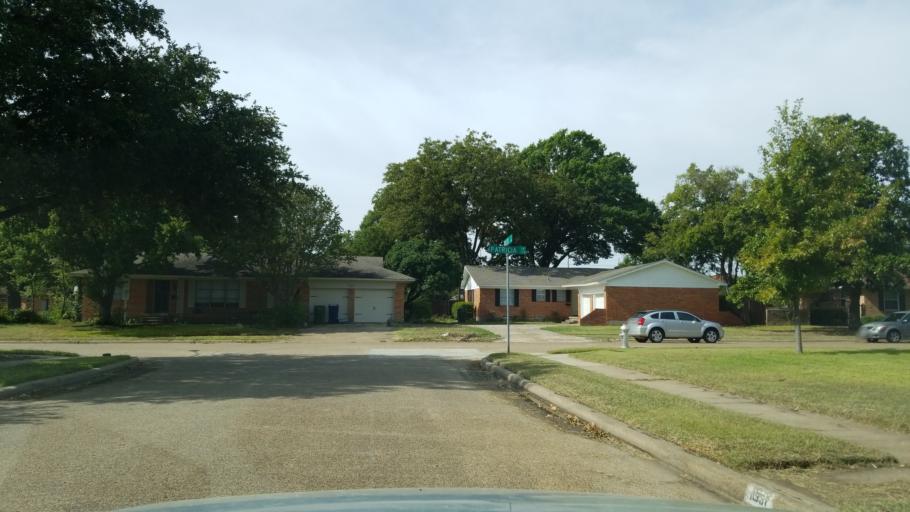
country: US
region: Texas
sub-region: Dallas County
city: Garland
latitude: 32.9005
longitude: -96.6634
